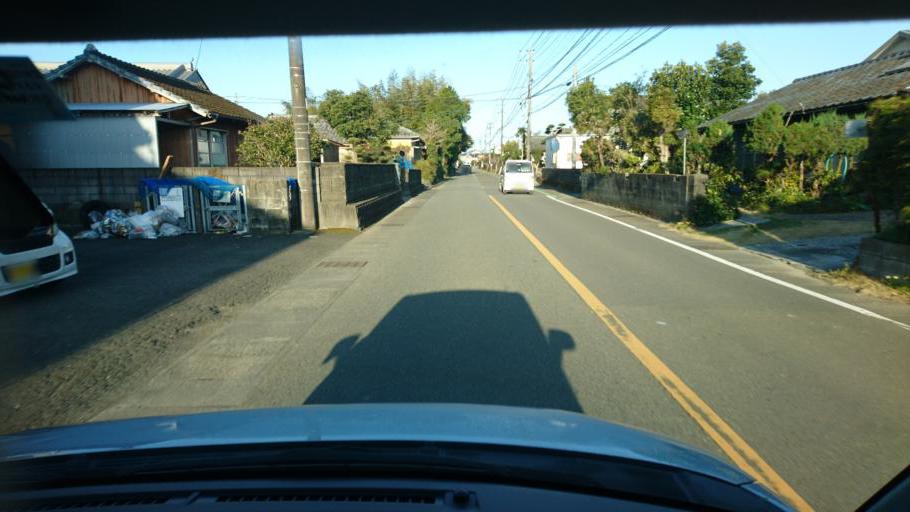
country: JP
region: Miyazaki
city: Miyazaki-shi
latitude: 31.8415
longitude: 131.4175
